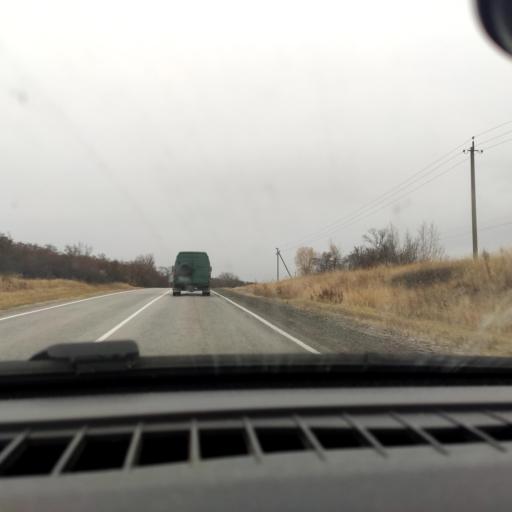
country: RU
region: Voronezj
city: Uryv-Pokrovka
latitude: 51.0742
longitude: 38.9955
